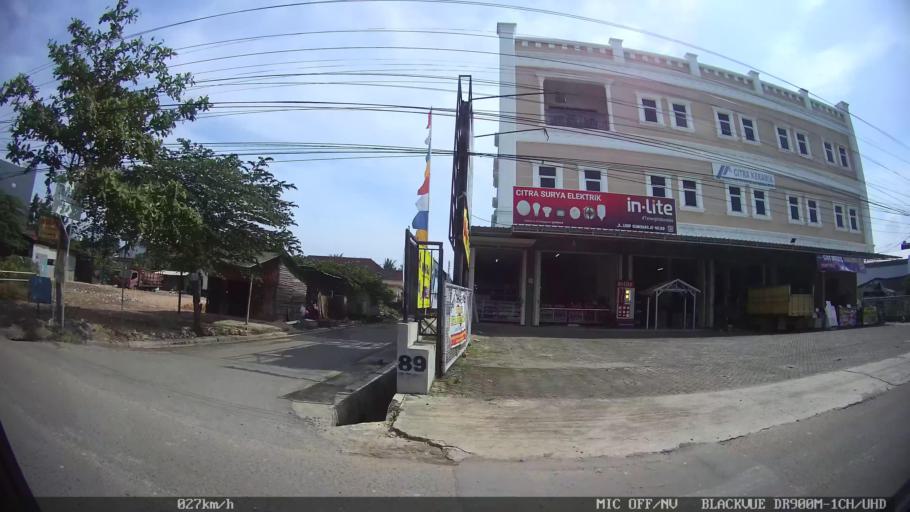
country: ID
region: Lampung
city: Kedaton
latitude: -5.3918
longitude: 105.2843
